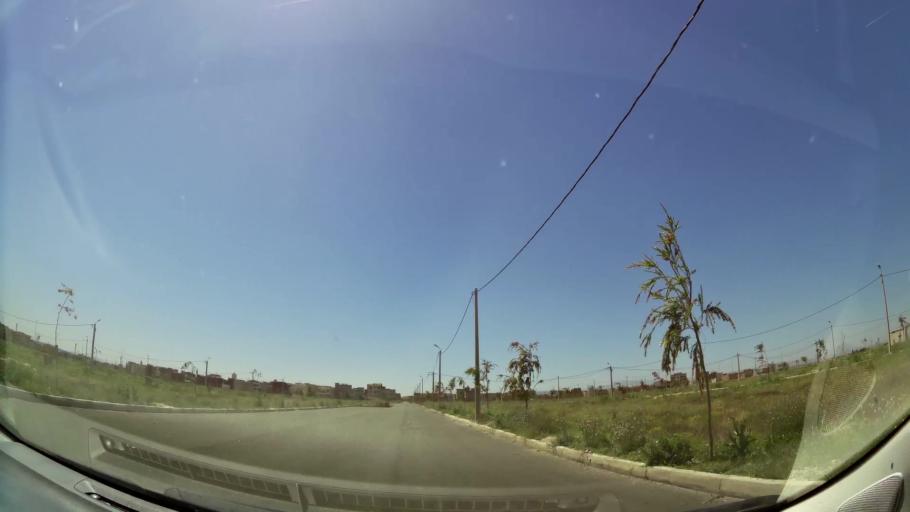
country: MA
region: Oriental
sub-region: Oujda-Angad
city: Oujda
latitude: 34.6828
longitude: -1.8593
